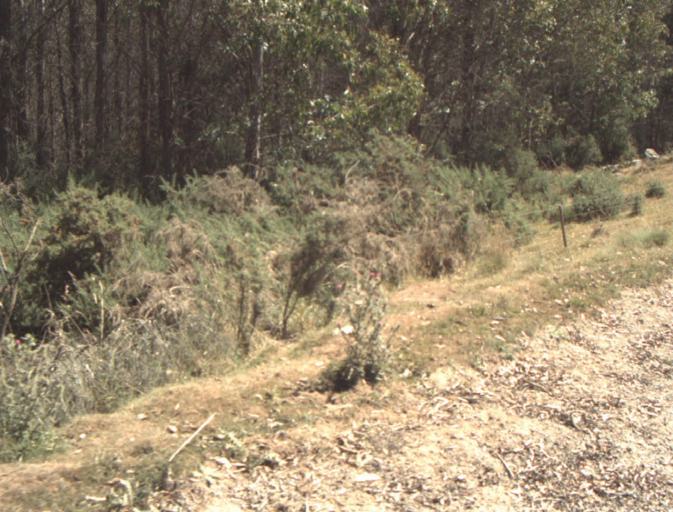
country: AU
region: Tasmania
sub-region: Dorset
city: Scottsdale
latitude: -41.3266
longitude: 147.4780
